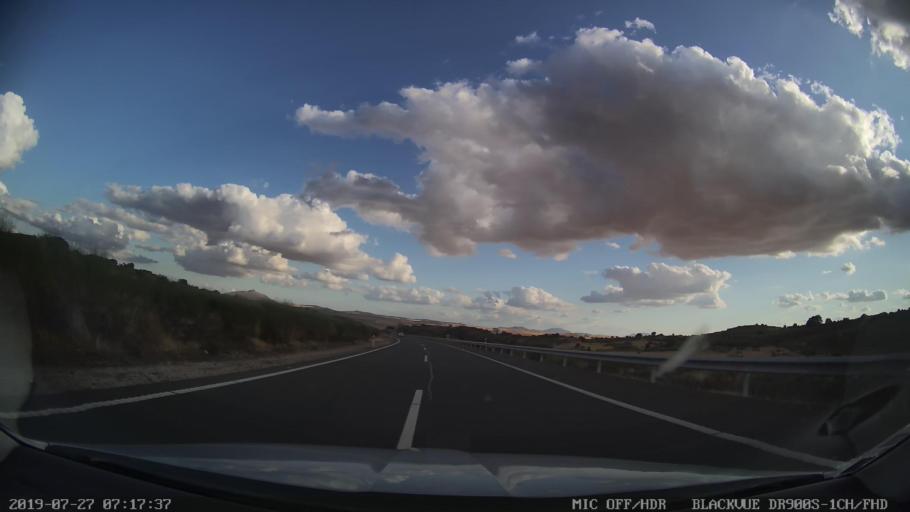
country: ES
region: Extremadura
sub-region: Provincia de Caceres
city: Trujillo
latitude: 39.4344
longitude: -5.8785
